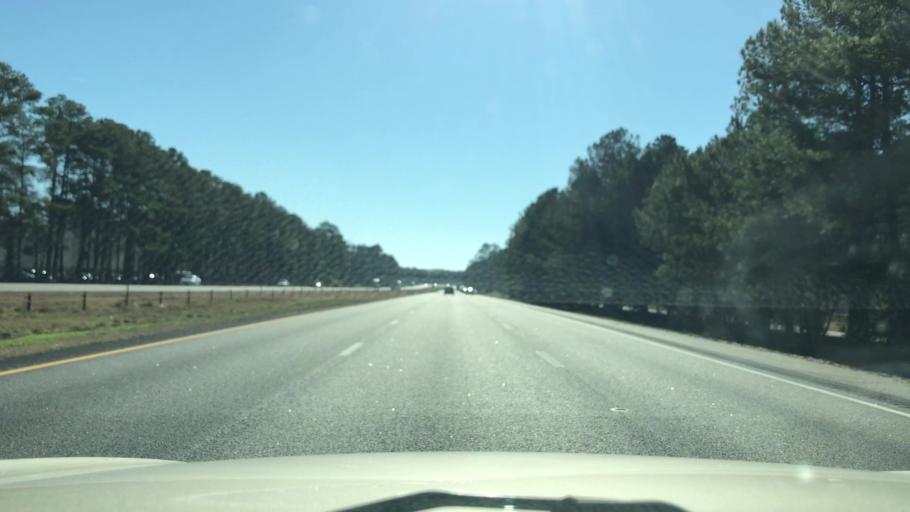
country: US
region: South Carolina
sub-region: Lexington County
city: Pineridge
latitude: 33.8960
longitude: -81.0451
